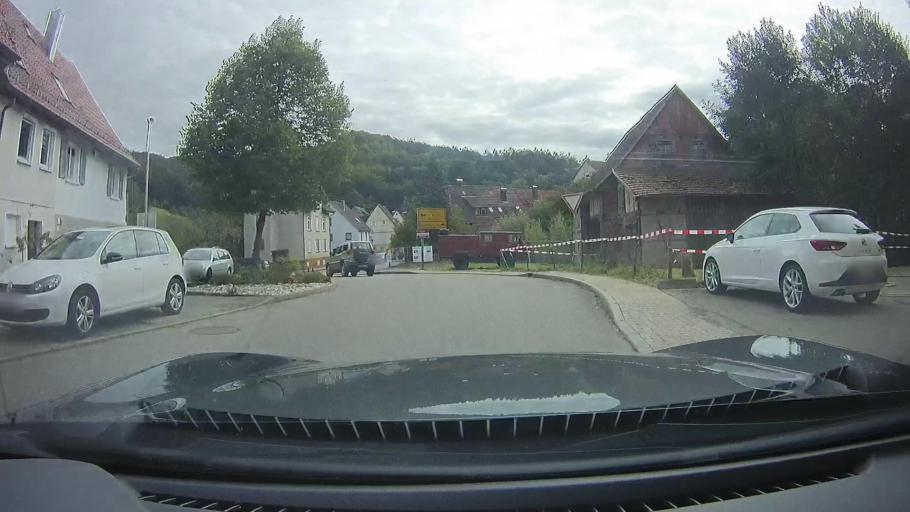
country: DE
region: Baden-Wuerttemberg
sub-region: Regierungsbezirk Stuttgart
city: Spiegelberg
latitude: 49.0398
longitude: 9.4452
